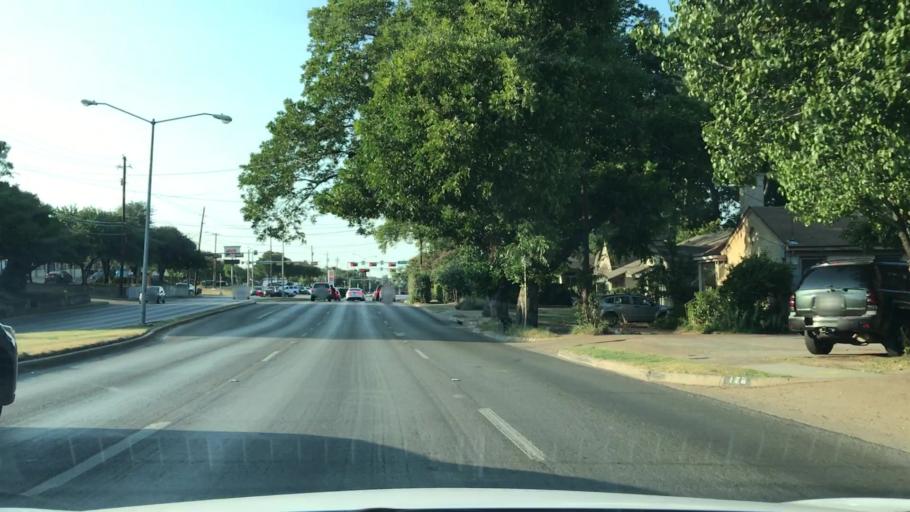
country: US
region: Texas
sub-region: Dallas County
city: Cockrell Hill
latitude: 32.7462
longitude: -96.8567
